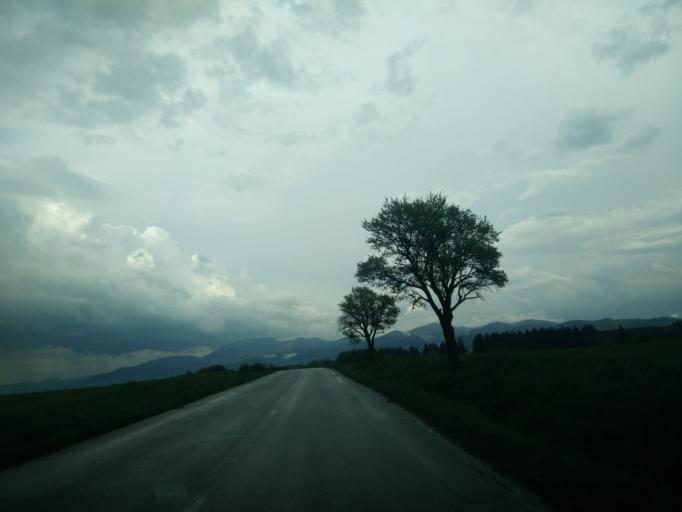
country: SK
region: Nitriansky
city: Handlova
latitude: 48.8675
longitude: 18.8118
